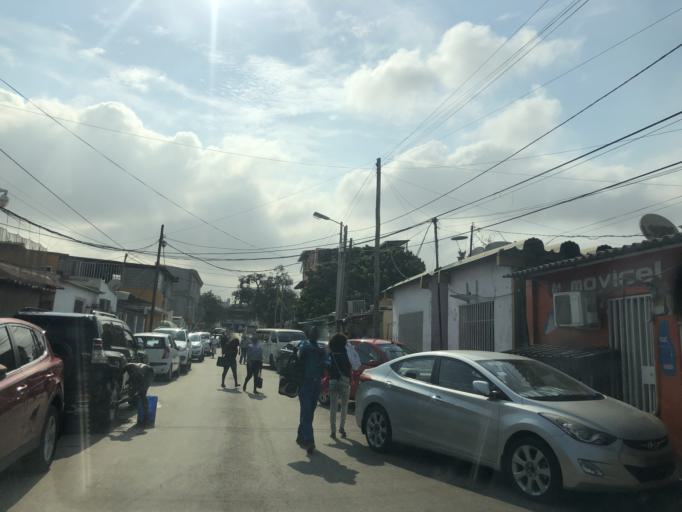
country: AO
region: Luanda
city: Luanda
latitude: -8.8290
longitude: 13.2244
